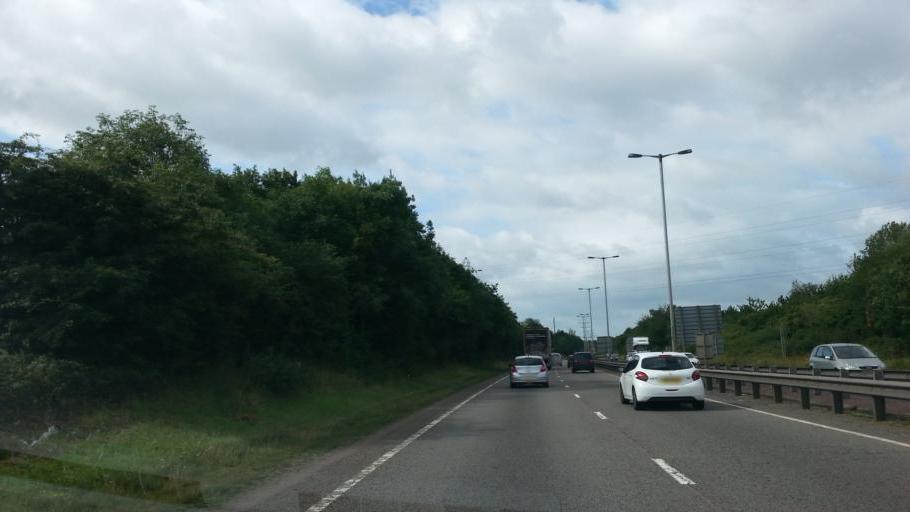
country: GB
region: England
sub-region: Warwickshire
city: Ryton on Dunsmore
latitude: 52.3944
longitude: -1.4327
